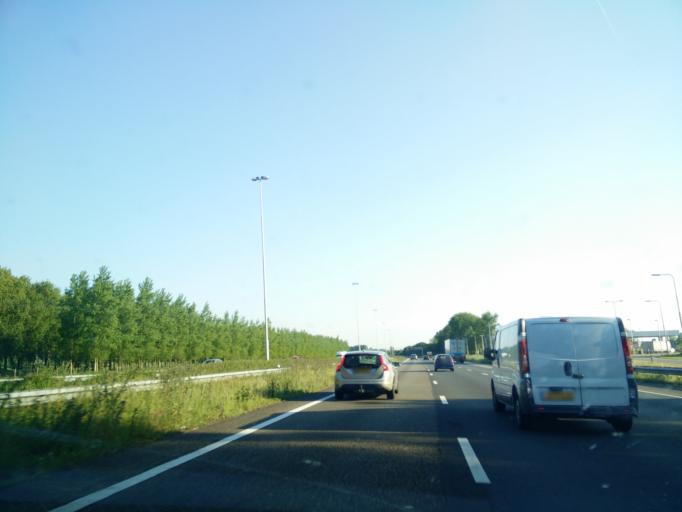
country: NL
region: South Holland
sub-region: Gemeente Zwijndrecht
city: Zwijndrecht
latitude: 51.7367
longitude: 4.6341
